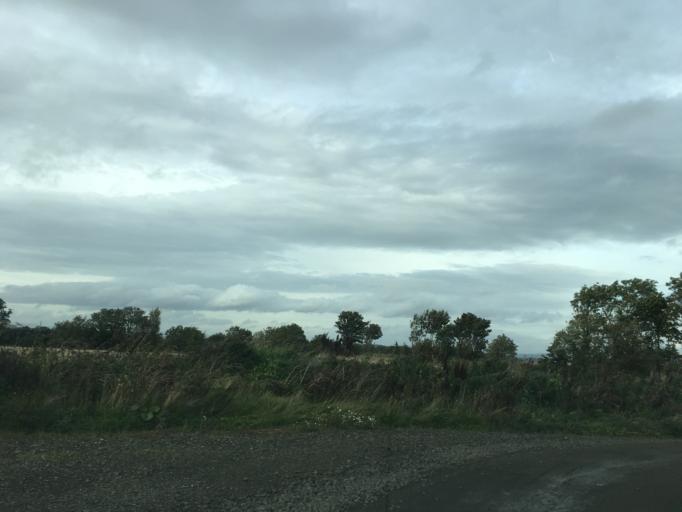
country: GB
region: Scotland
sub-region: West Lothian
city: Kirknewton
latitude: 55.9110
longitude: -3.4265
